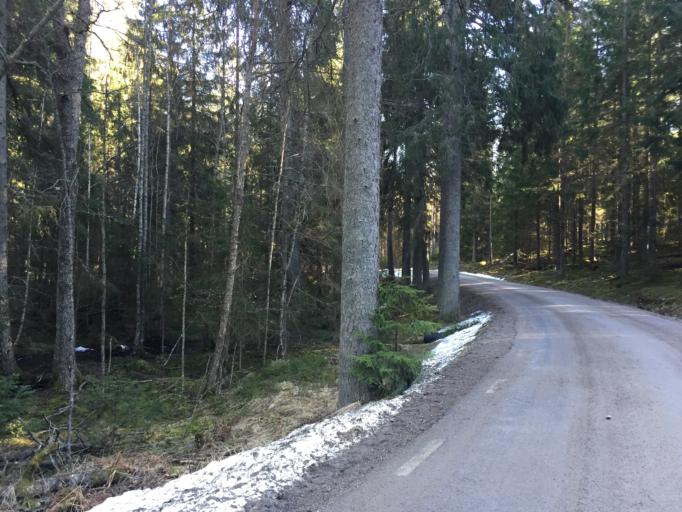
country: SE
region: OErebro
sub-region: Orebro Kommun
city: Odensbacken
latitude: 58.9731
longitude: 15.6421
